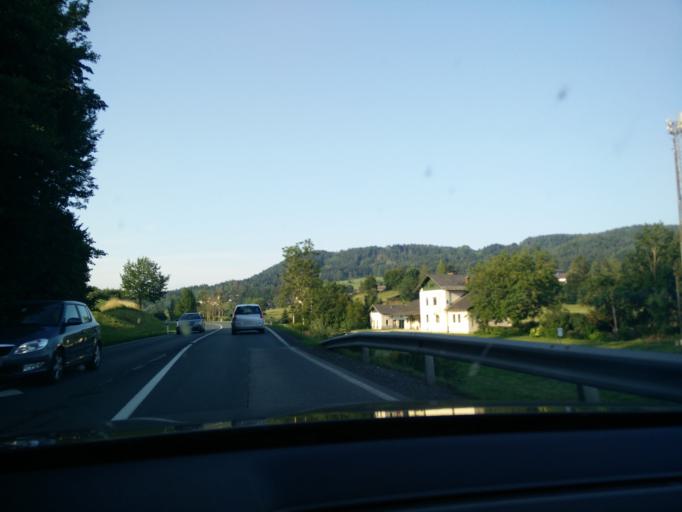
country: AT
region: Carinthia
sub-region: Politischer Bezirk Klagenfurt Land
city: Maria Rain
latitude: 46.5629
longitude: 14.2834
